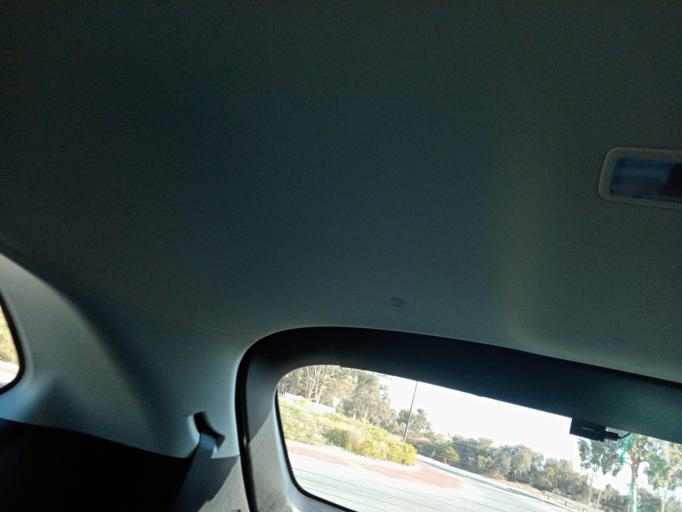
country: AU
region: Western Australia
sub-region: City of Cockburn
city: Beeliar
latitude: -32.1287
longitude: 115.8116
